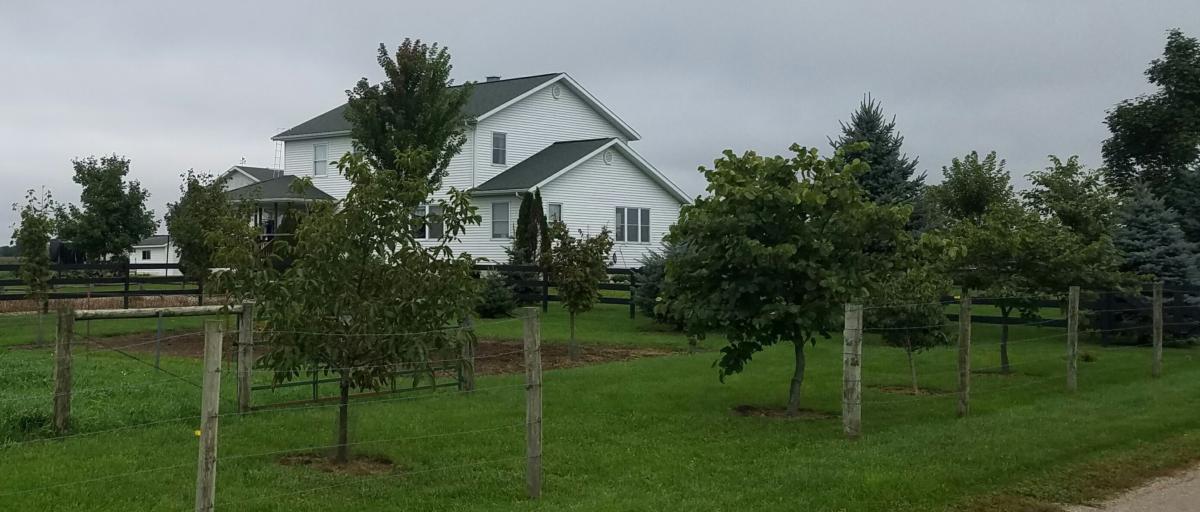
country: US
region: Indiana
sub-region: LaGrange County
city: Lagrange
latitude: 41.6841
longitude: -85.5280
